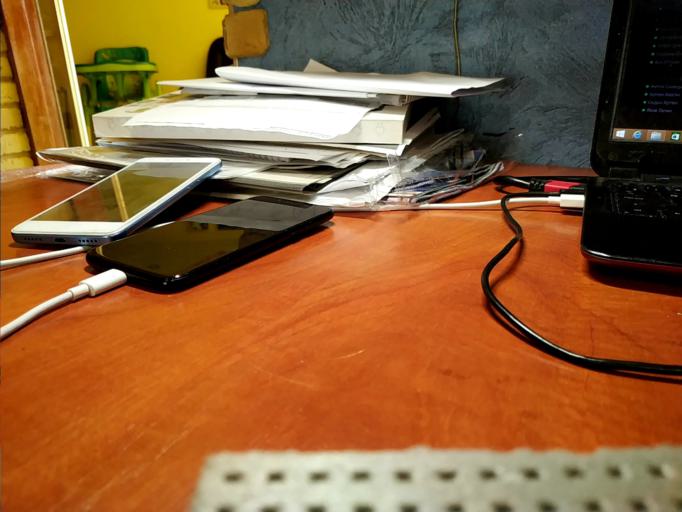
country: RU
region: Tverskaya
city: Spirovo
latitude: 57.4318
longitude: 35.0388
